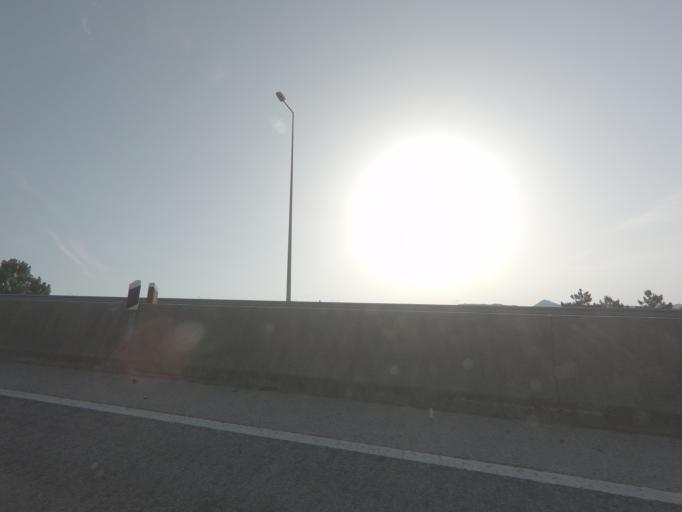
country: PT
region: Vila Real
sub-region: Sabrosa
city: Sabrosa
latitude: 41.2844
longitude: -7.4735
